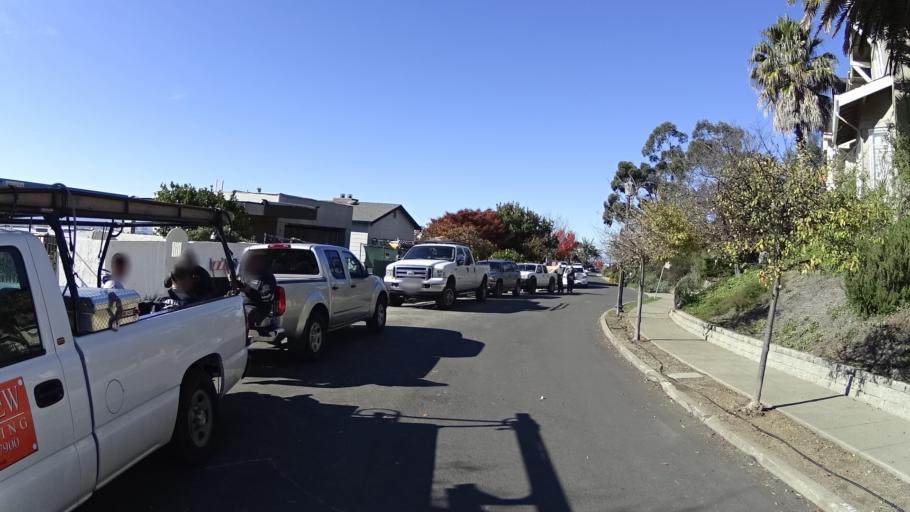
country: US
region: California
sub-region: Alameda County
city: Piedmont
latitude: 37.8433
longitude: -122.2289
